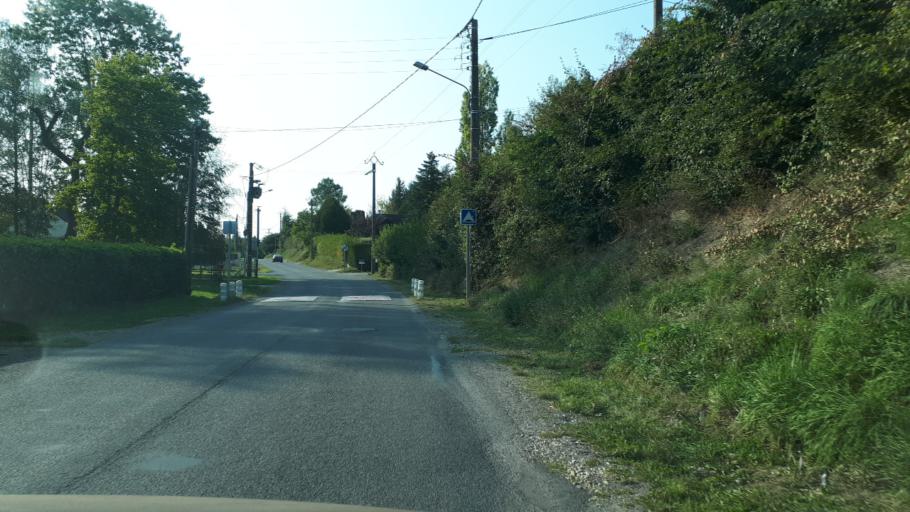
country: FR
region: Centre
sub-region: Departement du Cher
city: Vasselay
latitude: 47.2049
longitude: 2.4105
